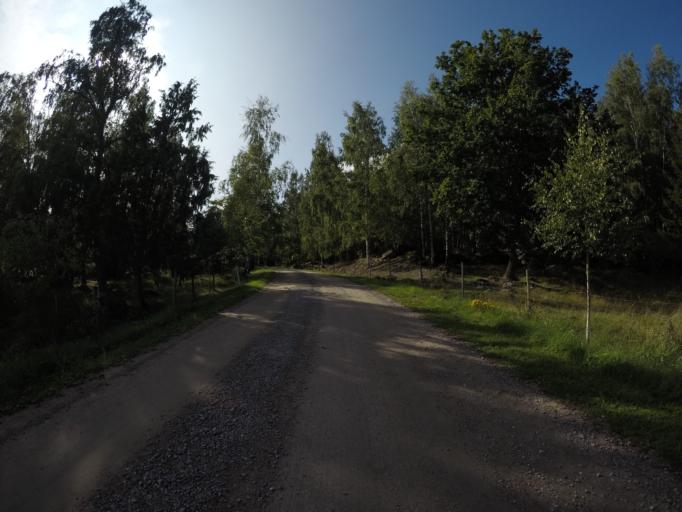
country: SE
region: Soedermanland
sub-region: Eskilstuna Kommun
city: Kvicksund
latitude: 59.5261
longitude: 16.3587
